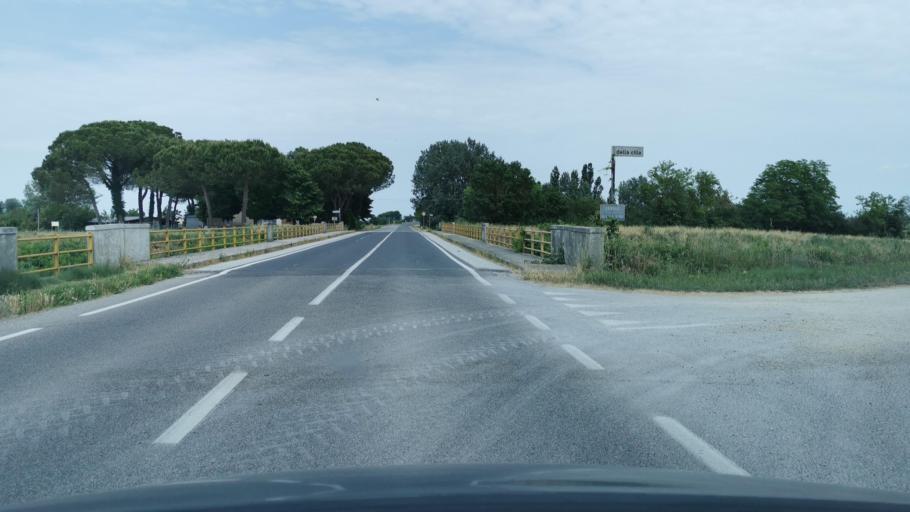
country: IT
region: Emilia-Romagna
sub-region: Provincia di Ravenna
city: Sant'Alberto
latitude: 44.5358
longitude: 12.1270
